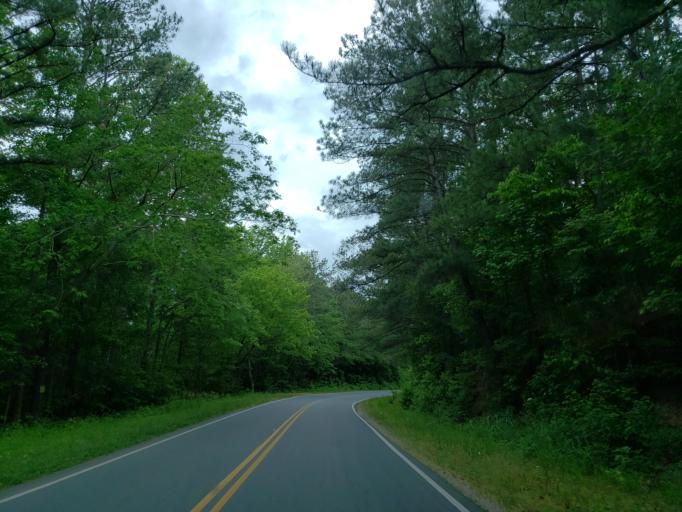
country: US
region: Georgia
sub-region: Polk County
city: Rockmart
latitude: 33.9558
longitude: -85.0436
